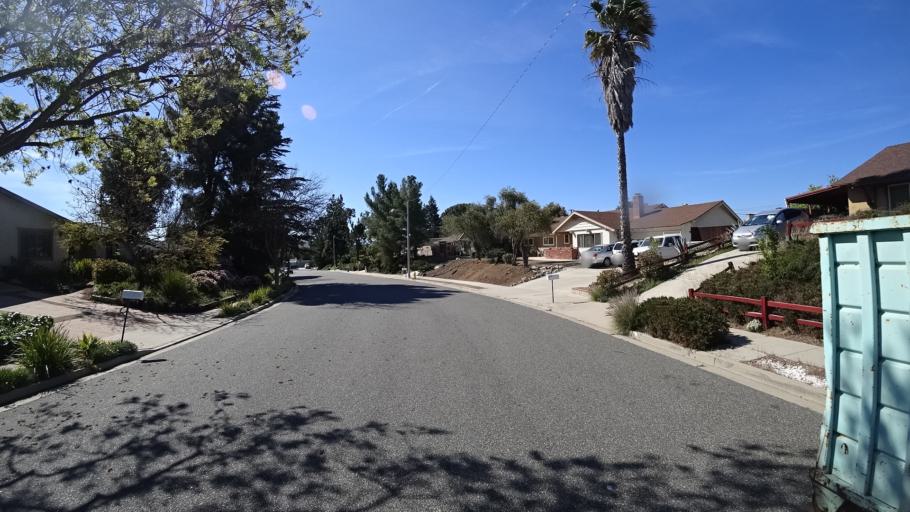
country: US
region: California
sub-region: Ventura County
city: Thousand Oaks
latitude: 34.2238
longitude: -118.8628
